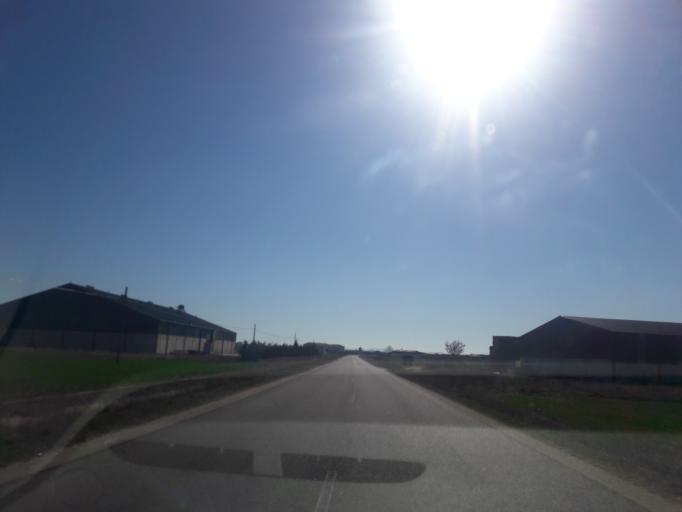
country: ES
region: Castille and Leon
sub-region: Provincia de Salamanca
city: Macotera
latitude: 40.8354
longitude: -5.3024
